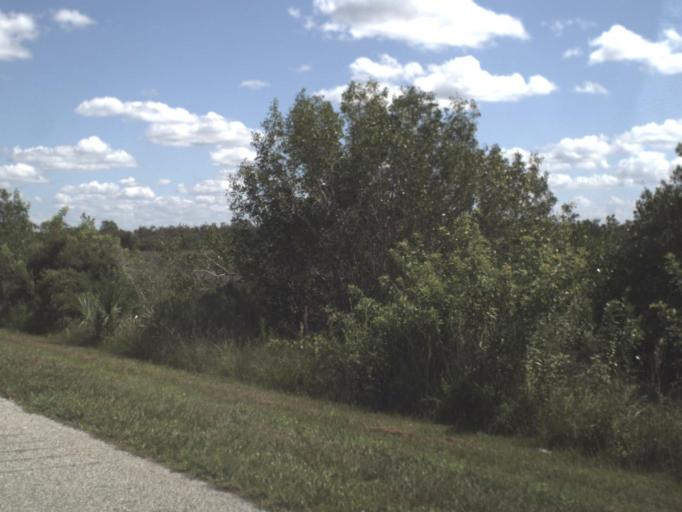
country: US
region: Florida
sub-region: Collier County
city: Marco
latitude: 25.9606
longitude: -81.4984
